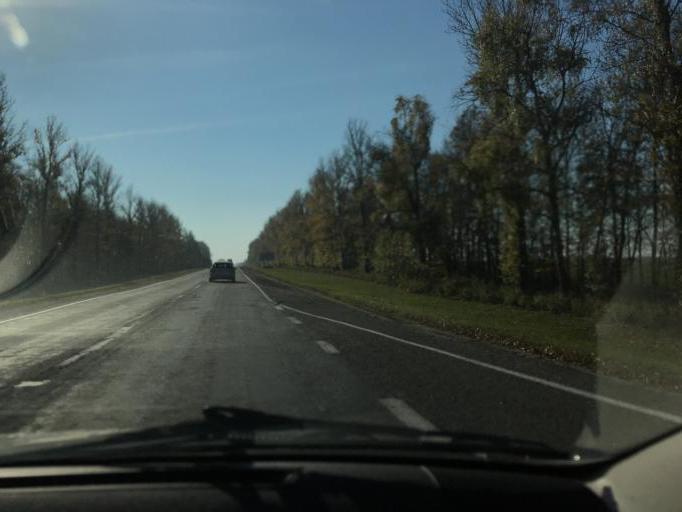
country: BY
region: Minsk
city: Salihorsk
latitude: 52.8998
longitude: 27.4753
